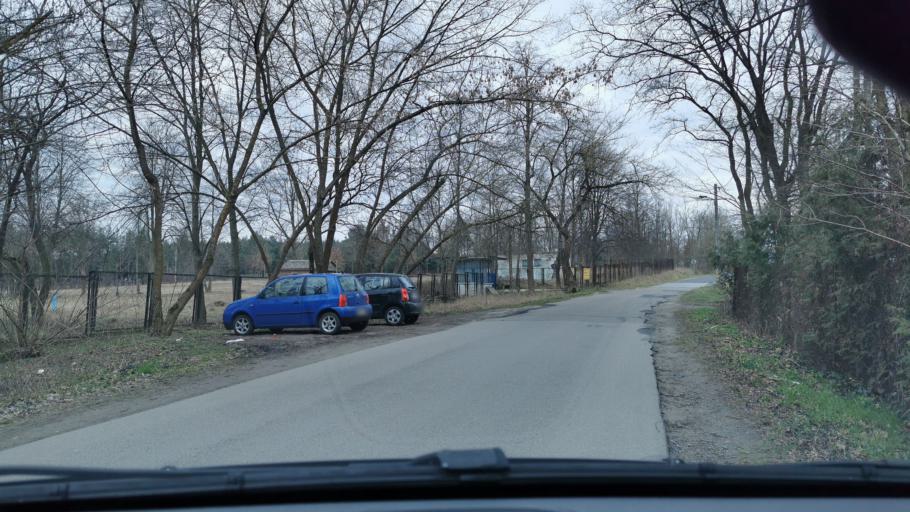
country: PL
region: Masovian Voivodeship
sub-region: Powiat zyrardowski
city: Radziejowice
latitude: 52.0100
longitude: 20.5206
